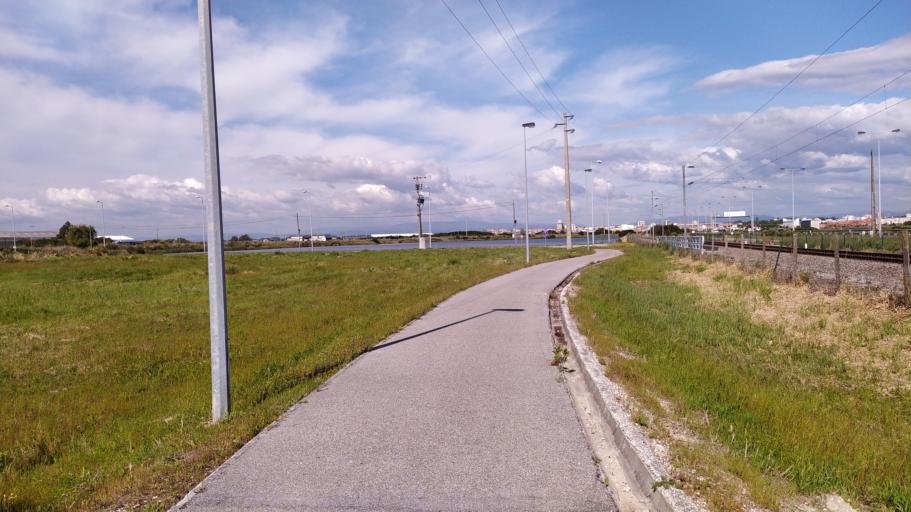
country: PT
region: Aveiro
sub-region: Ilhavo
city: Gafanha da Nazare
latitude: 40.6334
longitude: -8.6823
